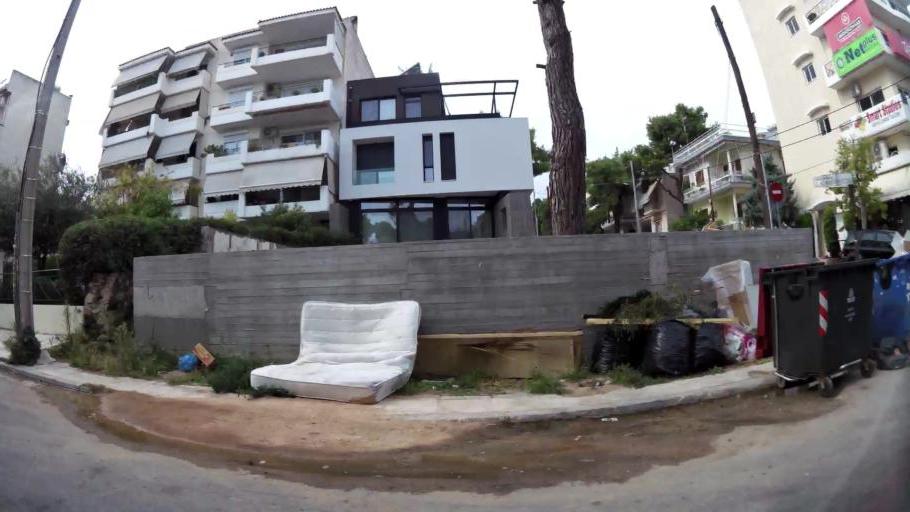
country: GR
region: Attica
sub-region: Nomarchia Athinas
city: Chaidari
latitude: 38.0139
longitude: 23.6496
